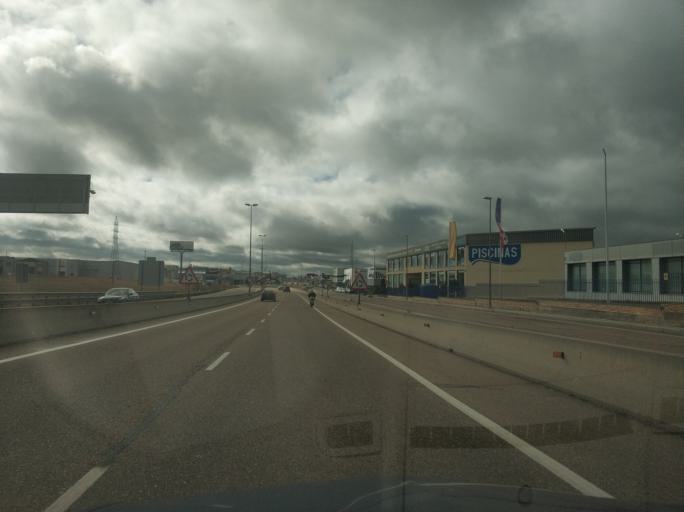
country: ES
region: Castille and Leon
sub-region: Provincia de Salamanca
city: Villares de la Reina
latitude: 40.9977
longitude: -5.6314
